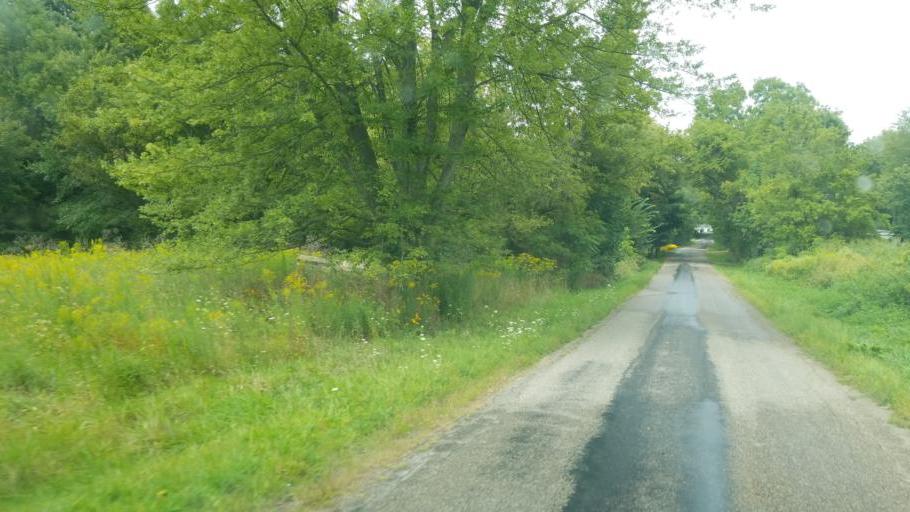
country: US
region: Ohio
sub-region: Ashland County
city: Loudonville
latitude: 40.6232
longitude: -82.3509
